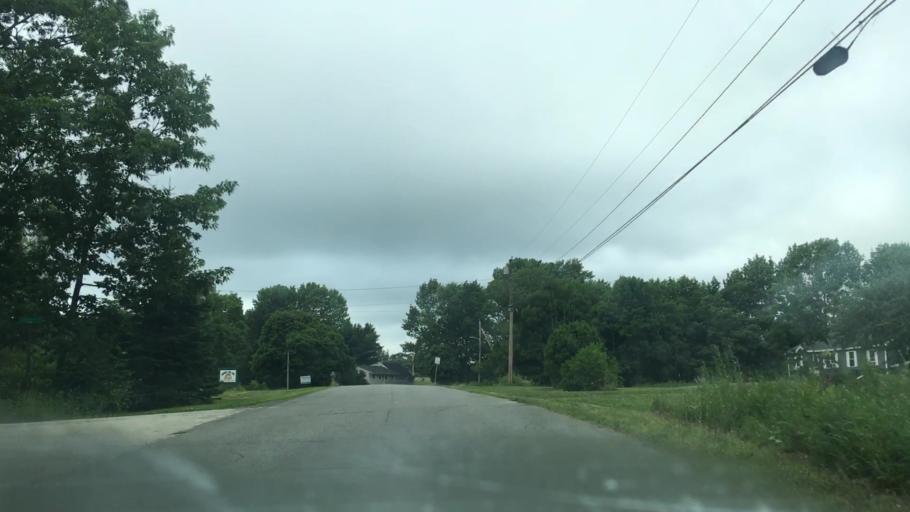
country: US
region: Maine
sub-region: Penobscot County
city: Veazie
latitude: 44.8461
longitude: -68.7466
